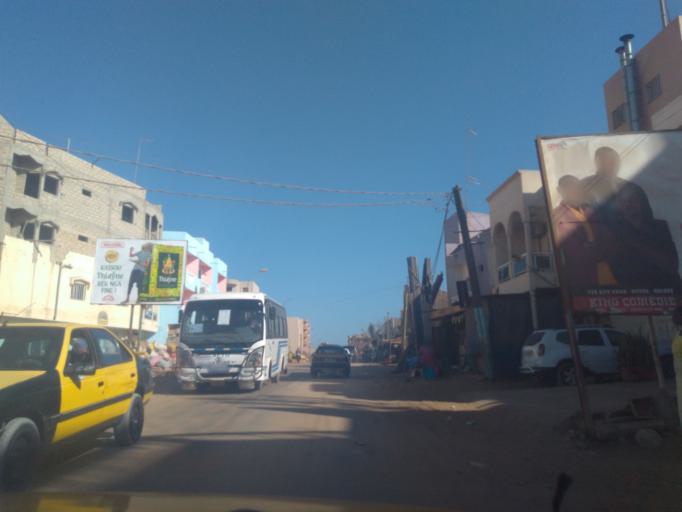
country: SN
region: Dakar
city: Pikine
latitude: 14.7716
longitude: -17.4172
